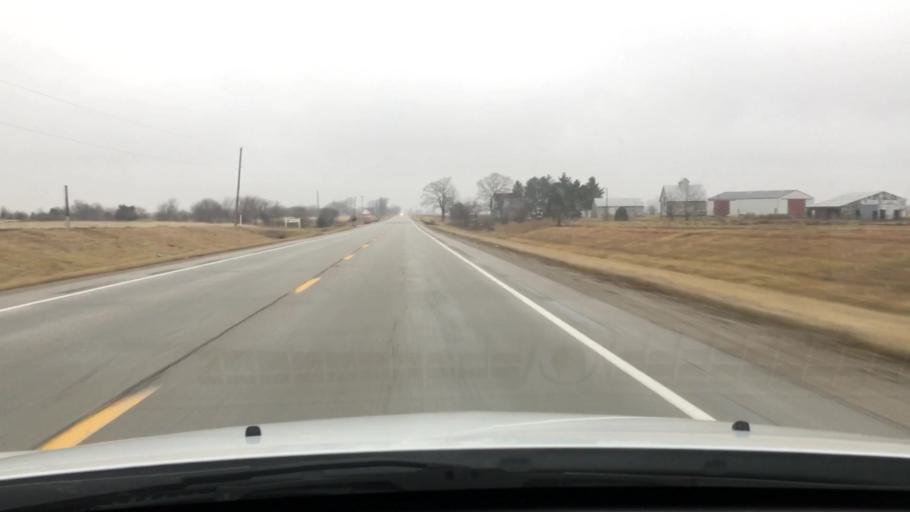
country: US
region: Illinois
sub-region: Livingston County
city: Pontiac
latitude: 40.8726
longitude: -88.7428
